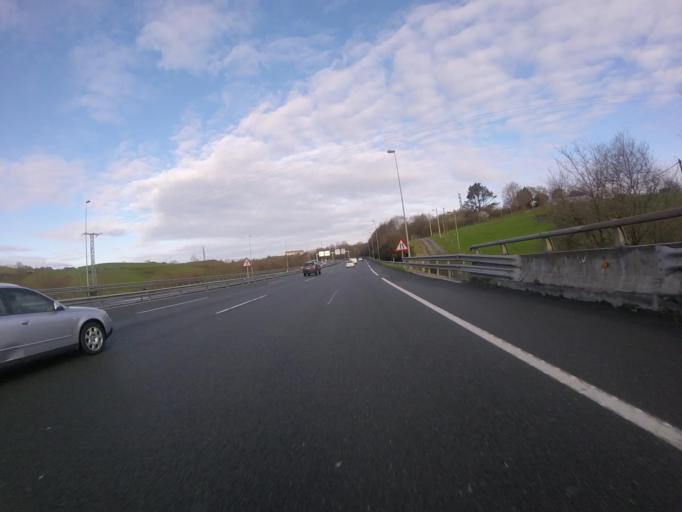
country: ES
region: Basque Country
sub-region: Provincia de Guipuzcoa
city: Pasaia
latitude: 43.3082
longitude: -1.9278
